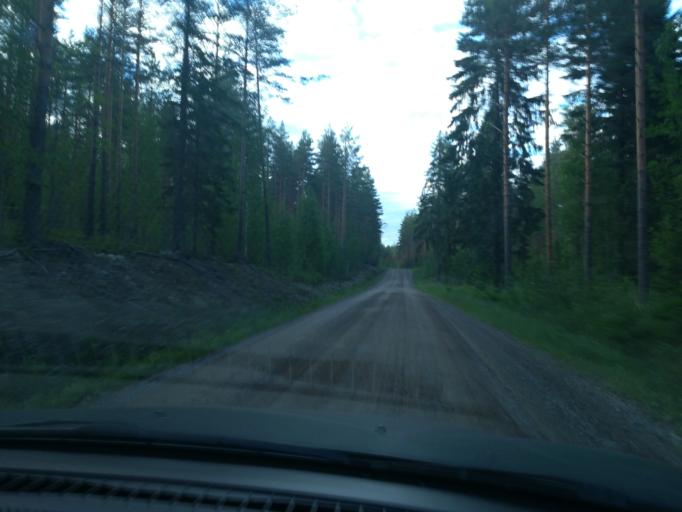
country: FI
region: Southern Savonia
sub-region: Mikkeli
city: Puumala
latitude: 61.5800
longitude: 28.1639
